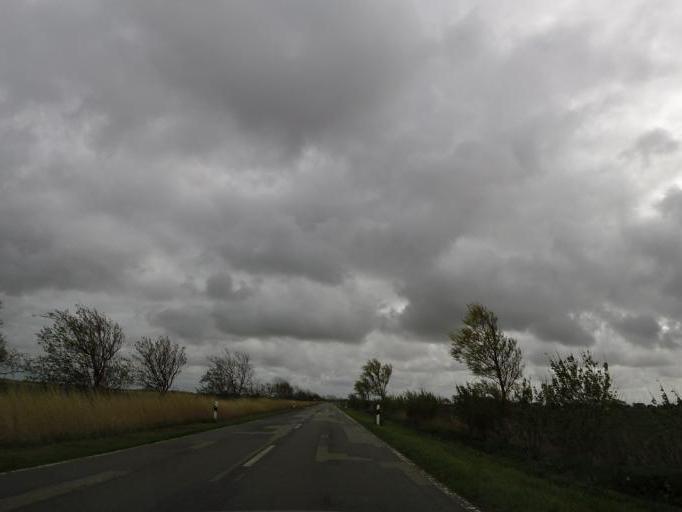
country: DE
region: Schleswig-Holstein
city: Galmsbull
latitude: 54.7584
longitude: 8.7520
